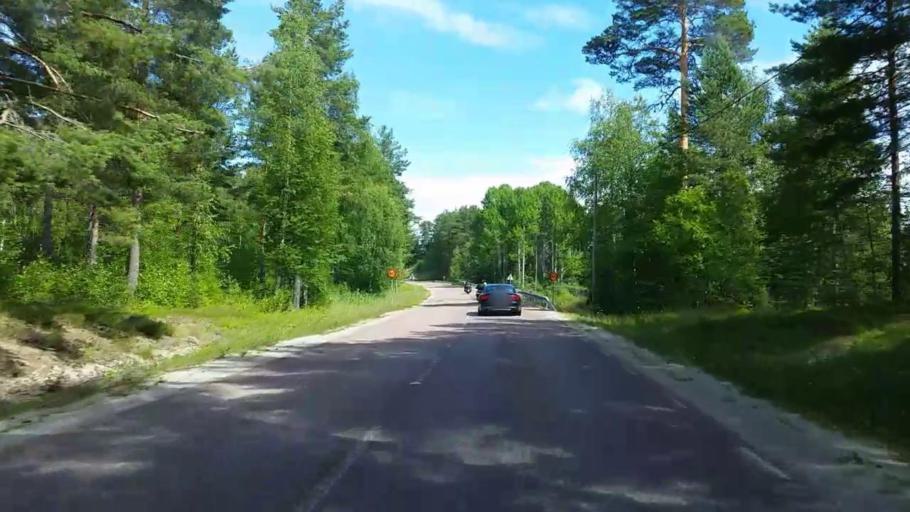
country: SE
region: Dalarna
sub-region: Rattviks Kommun
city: Vikarbyn
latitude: 61.1695
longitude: 15.1461
